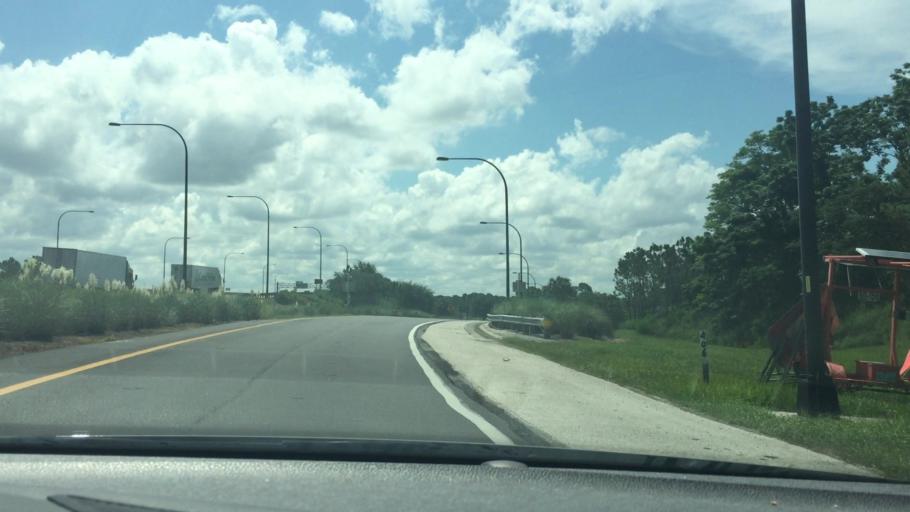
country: US
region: Florida
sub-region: Orange County
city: Pine Hills
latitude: 28.5498
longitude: -81.4604
